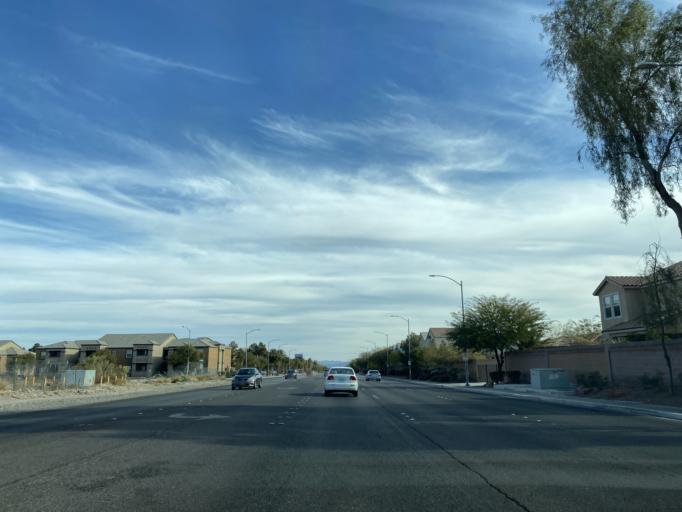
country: US
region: Nevada
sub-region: Clark County
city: Enterprise
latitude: 36.0559
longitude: -115.2397
